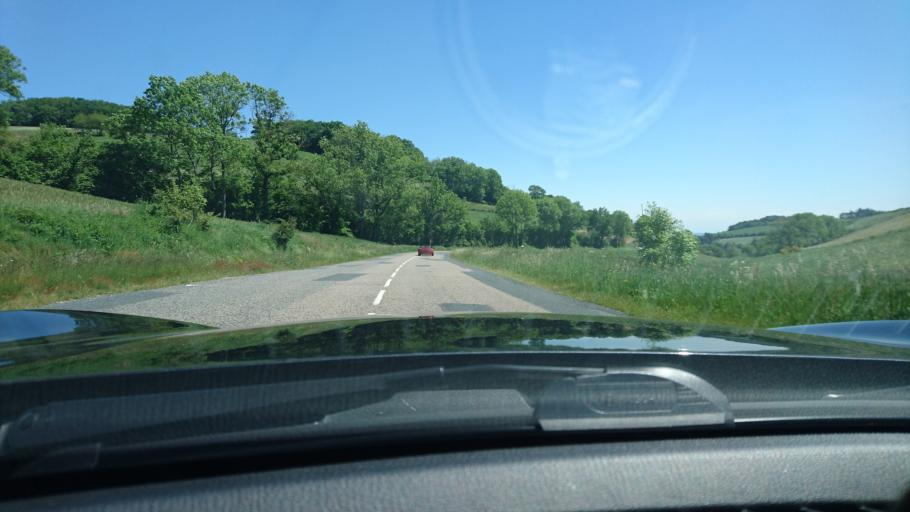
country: FR
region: Rhone-Alpes
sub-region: Departement du Rhone
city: Courzieu
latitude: 45.7189
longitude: 4.5712
